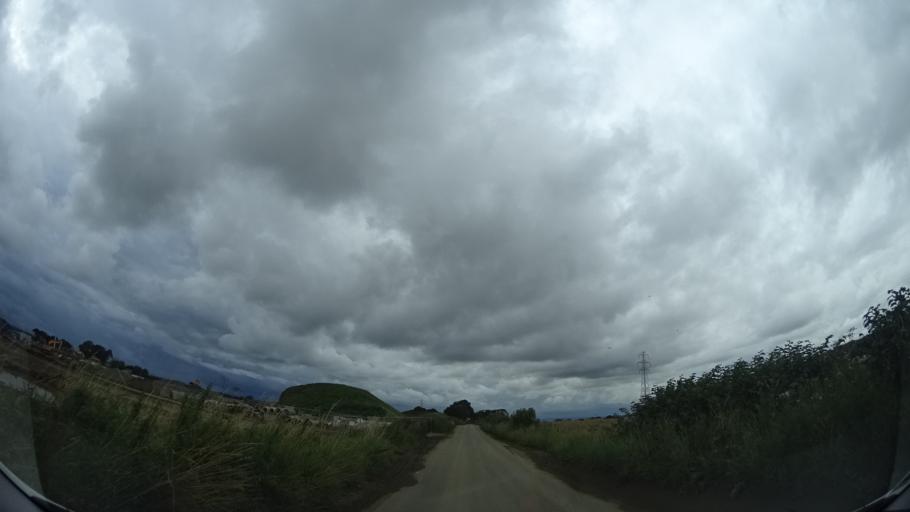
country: GB
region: Scotland
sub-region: West Lothian
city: Kirknewton
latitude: 55.9024
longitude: -3.4342
